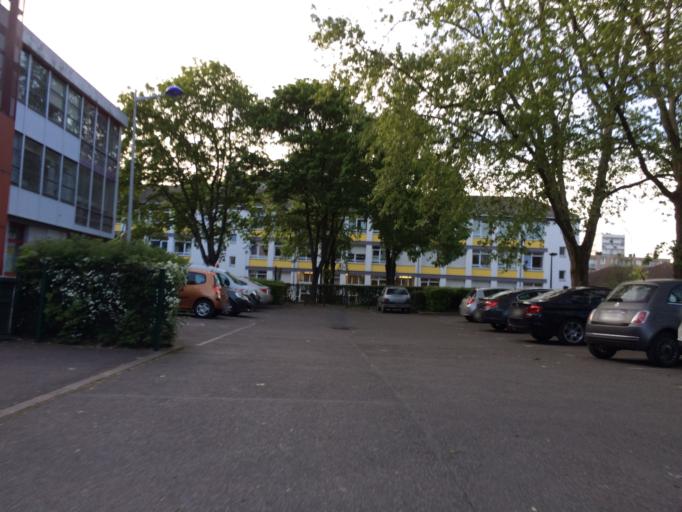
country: FR
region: Ile-de-France
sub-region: Departement de l'Essonne
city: Massy
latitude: 48.7326
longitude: 2.2922
